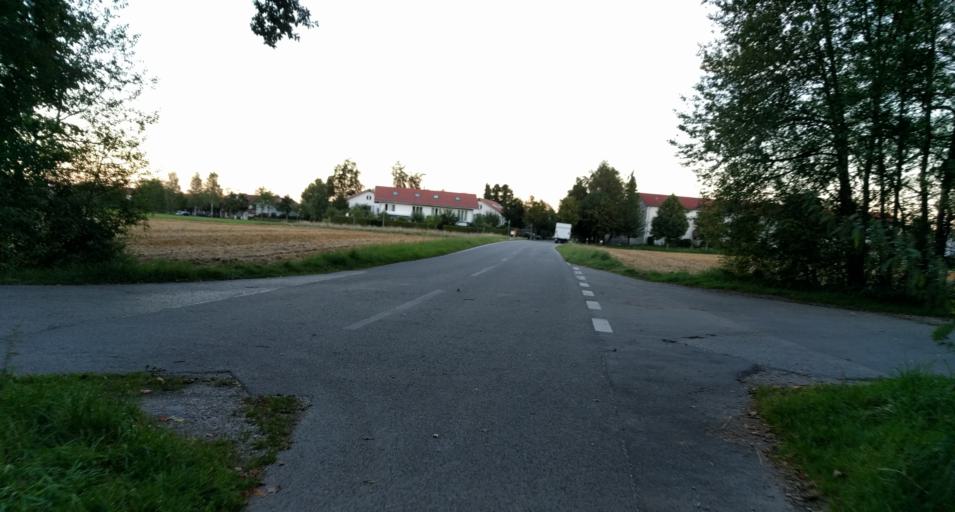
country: DE
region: Bavaria
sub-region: Upper Bavaria
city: Oberhaching
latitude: 48.0251
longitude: 11.5698
